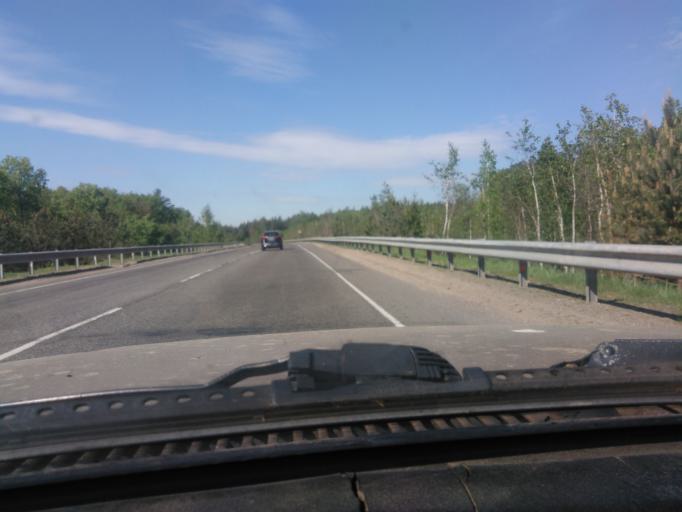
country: BY
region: Mogilev
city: Myazhysyatki
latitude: 53.8080
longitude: 30.2142
